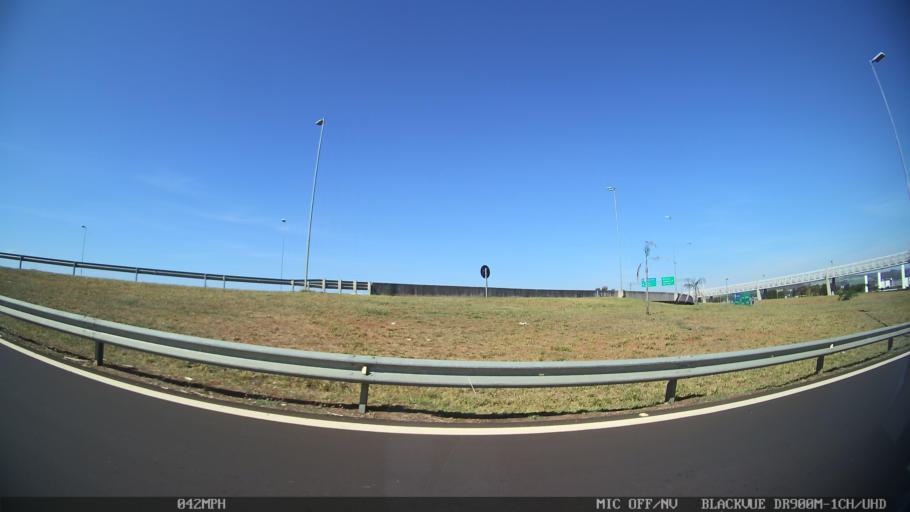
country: BR
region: Sao Paulo
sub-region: Ribeirao Preto
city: Ribeirao Preto
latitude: -21.2066
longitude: -47.7605
